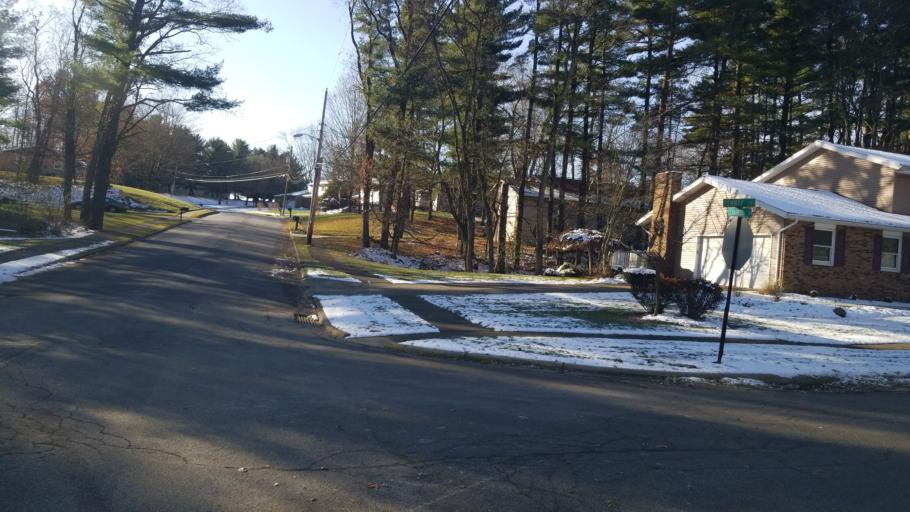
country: US
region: Ohio
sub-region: Richland County
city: Lexington
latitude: 40.6711
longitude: -82.5983
